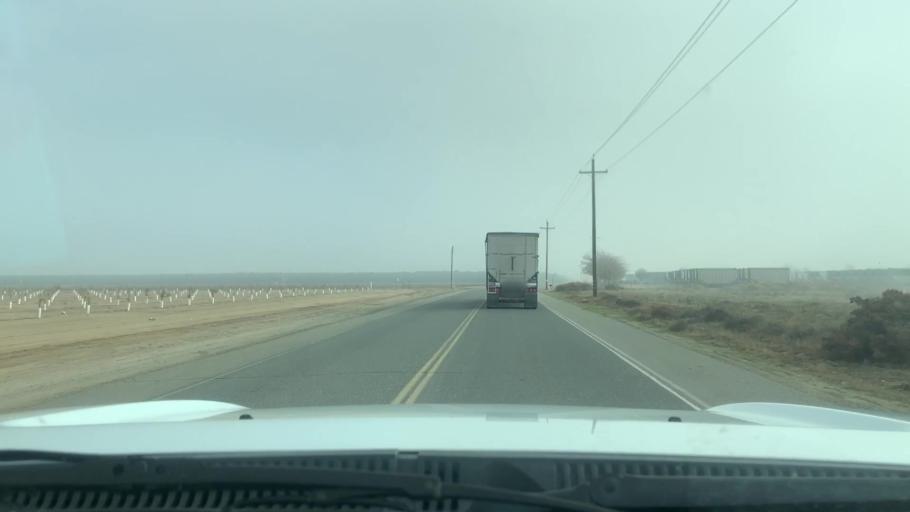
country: US
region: California
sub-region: Kern County
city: Buttonwillow
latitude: 35.5007
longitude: -119.5297
